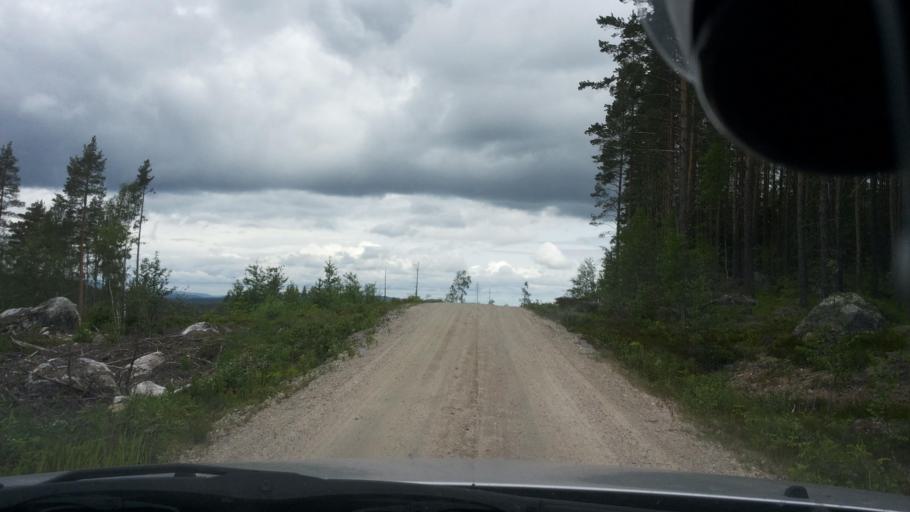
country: SE
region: Gaevleborg
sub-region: Ovanakers Kommun
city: Edsbyn
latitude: 61.4767
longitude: 15.3114
